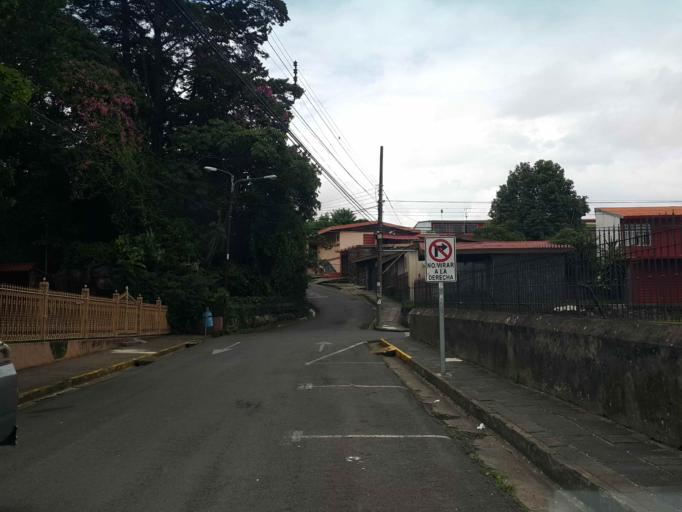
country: CR
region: Heredia
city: Mercedes
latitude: 10.0213
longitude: -84.1232
